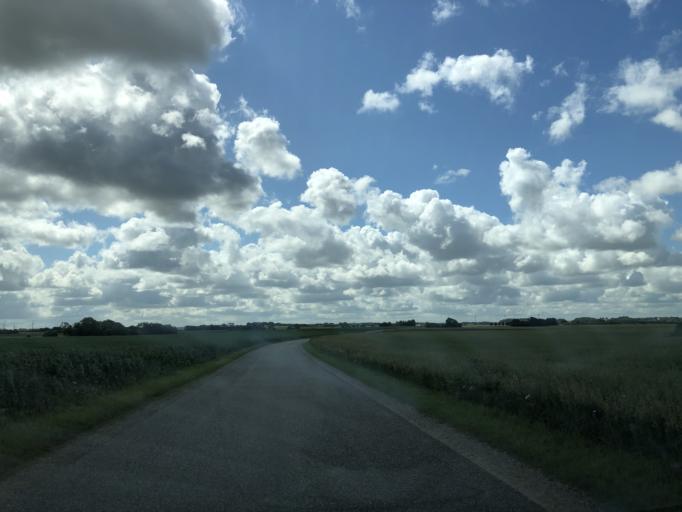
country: DK
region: Central Jutland
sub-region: Struer Kommune
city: Struer
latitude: 56.4574
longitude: 8.5235
